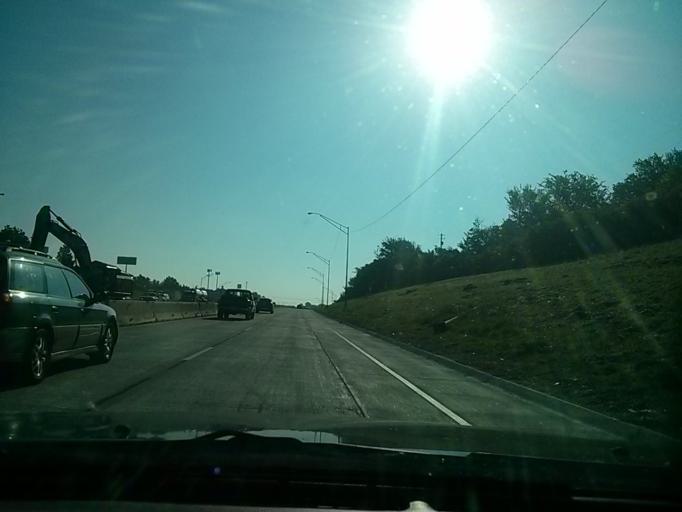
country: US
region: Oklahoma
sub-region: Tulsa County
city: Tulsa
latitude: 36.1593
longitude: -95.9301
